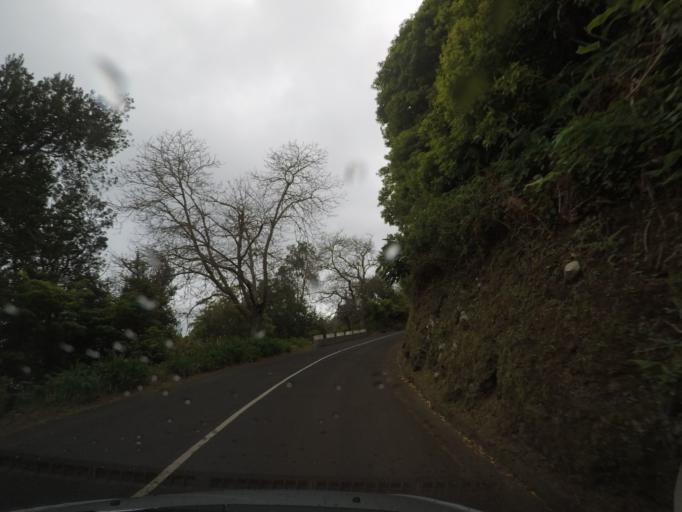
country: PT
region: Madeira
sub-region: Santana
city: Santana
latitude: 32.7502
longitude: -16.8337
